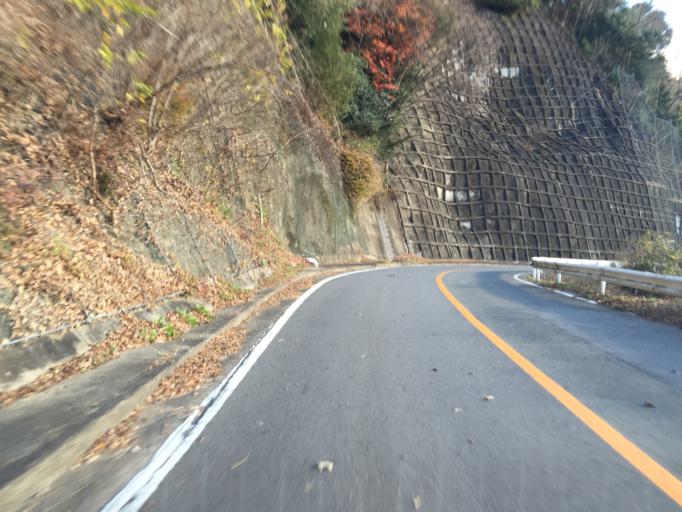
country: JP
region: Fukushima
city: Iwaki
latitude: 37.1442
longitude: 140.8380
